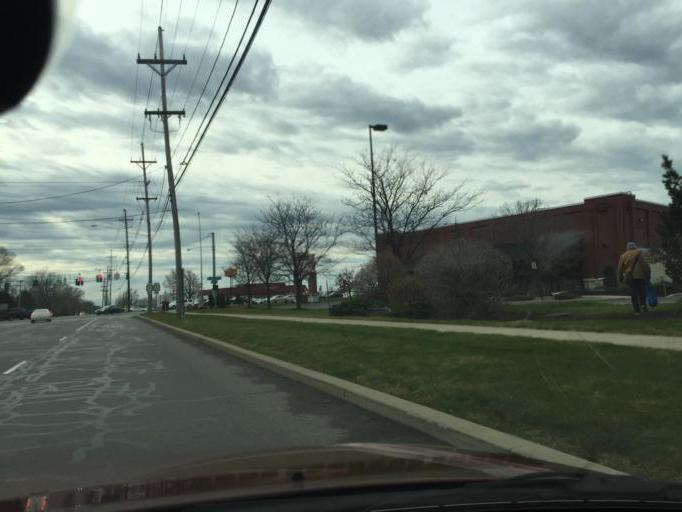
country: US
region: New York
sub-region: Monroe County
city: Rochester
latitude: 43.0881
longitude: -77.6169
